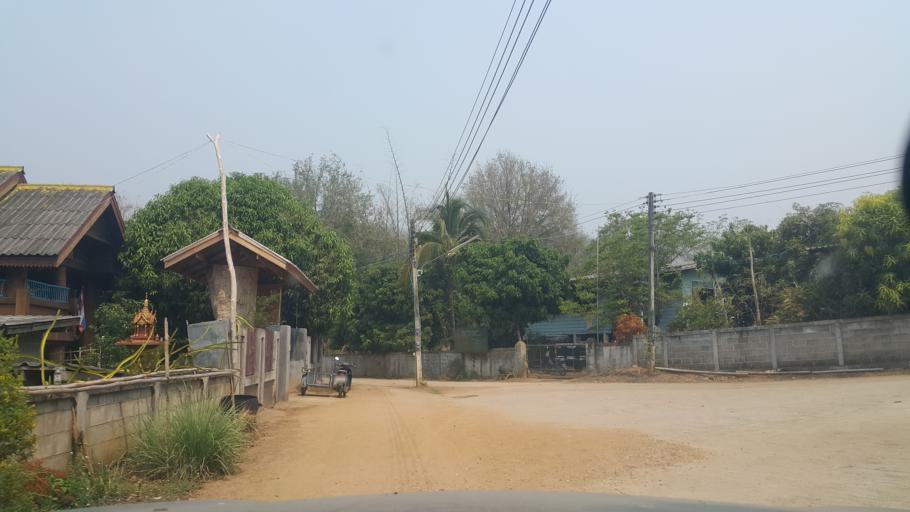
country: TH
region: Lampang
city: Sop Prap
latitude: 17.8062
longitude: 99.2566
